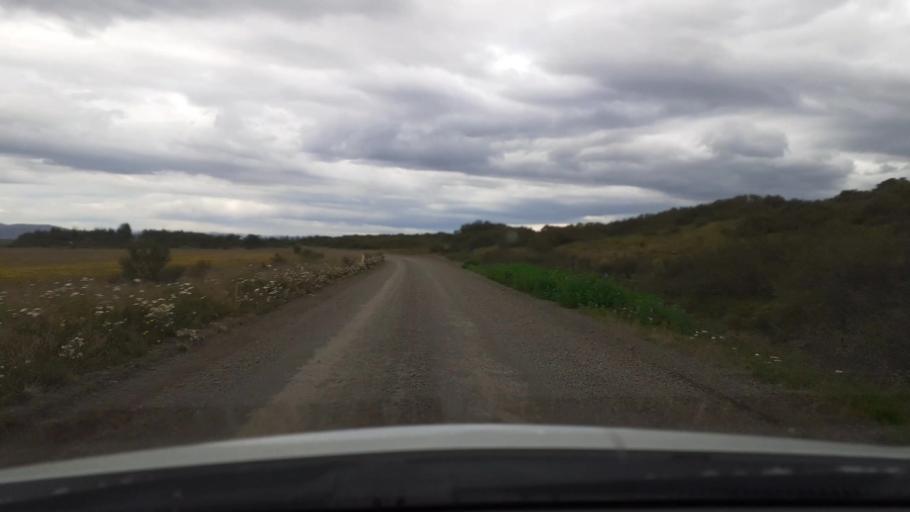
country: IS
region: West
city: Borgarnes
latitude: 64.6096
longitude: -21.9566
